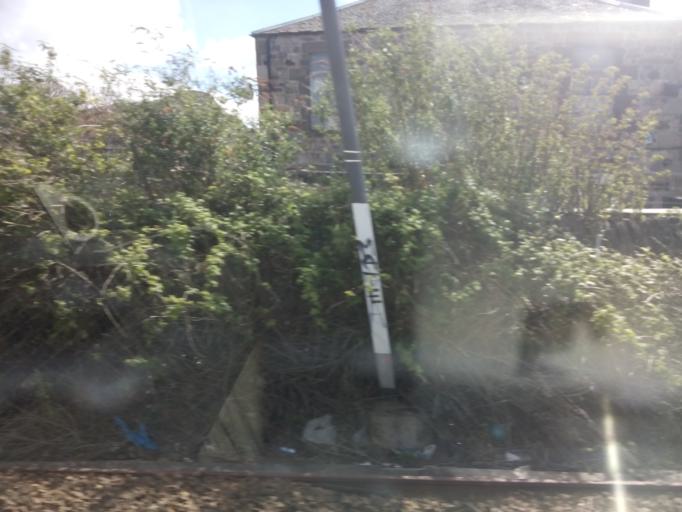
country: GB
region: Scotland
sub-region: West Lothian
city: Seafield
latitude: 55.9557
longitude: -3.1663
